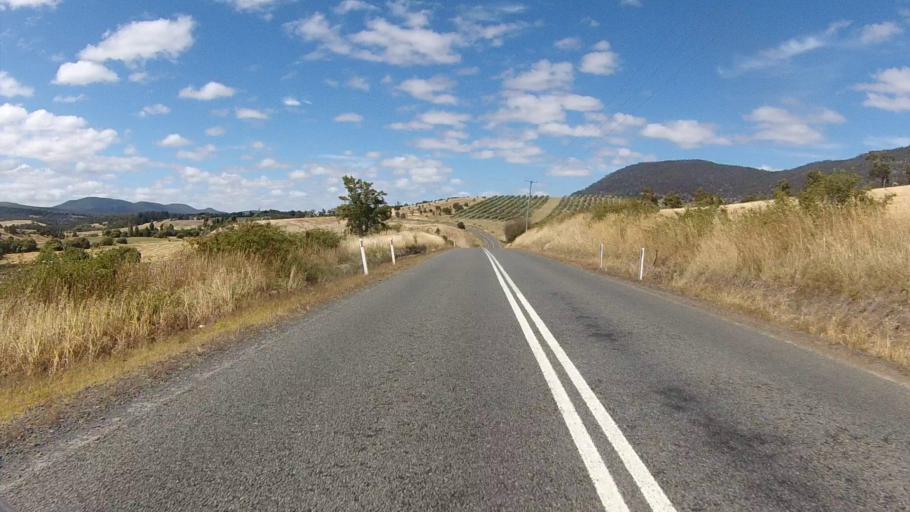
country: AU
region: Tasmania
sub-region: Brighton
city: Old Beach
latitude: -42.6003
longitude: 147.4162
